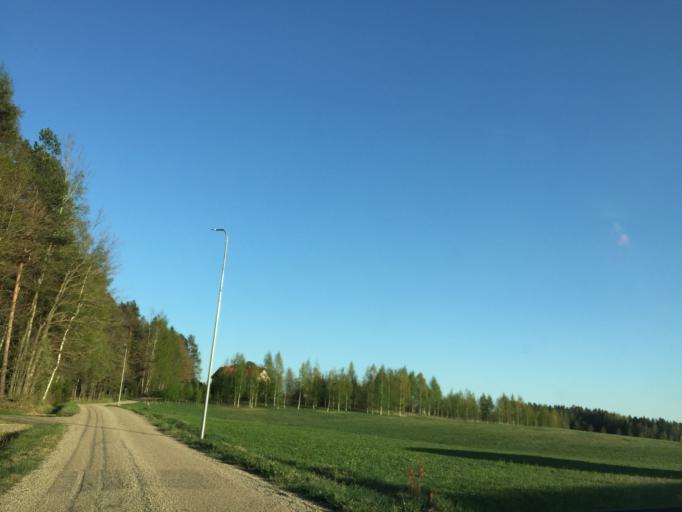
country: LV
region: Koknese
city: Koknese
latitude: 56.7197
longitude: 25.4791
